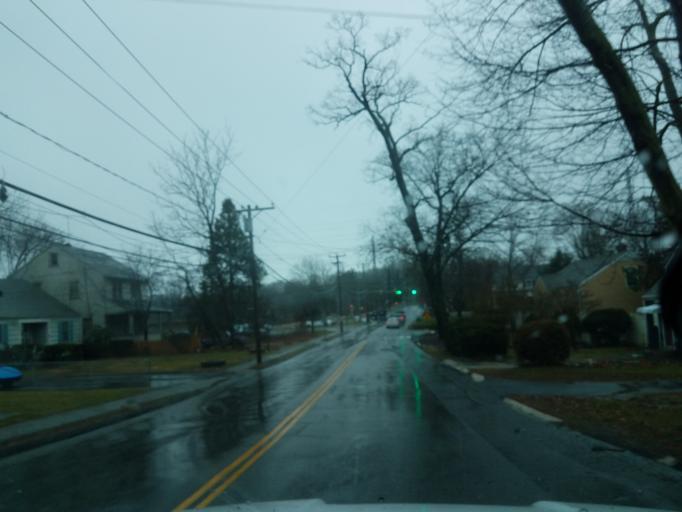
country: US
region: Connecticut
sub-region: Fairfield County
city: Darien
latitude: 41.0706
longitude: -73.4990
